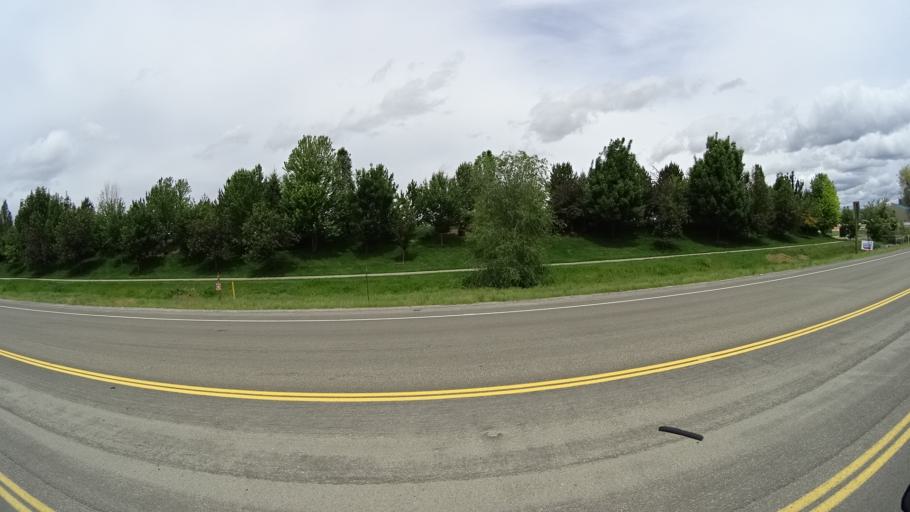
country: US
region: Idaho
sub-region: Ada County
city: Eagle
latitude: 43.6935
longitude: -116.4169
